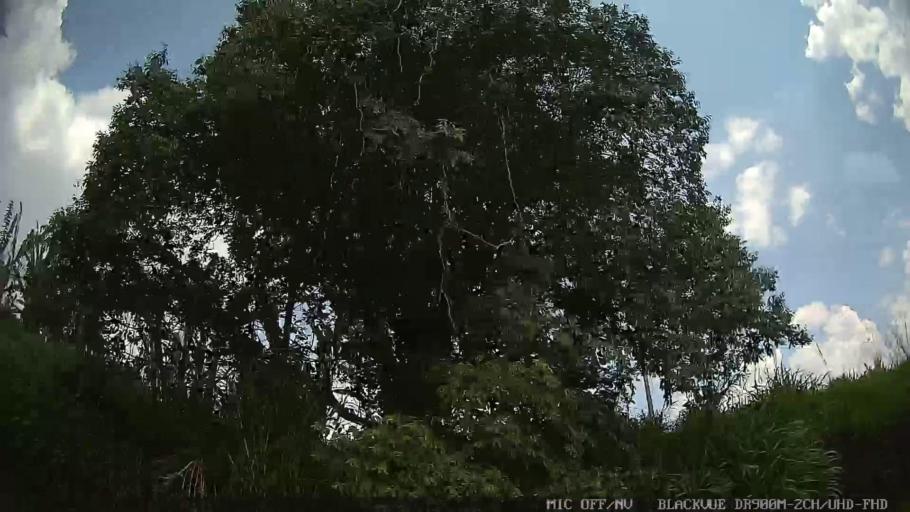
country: BR
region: Sao Paulo
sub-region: Itatiba
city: Itatiba
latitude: -22.9620
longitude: -46.7124
